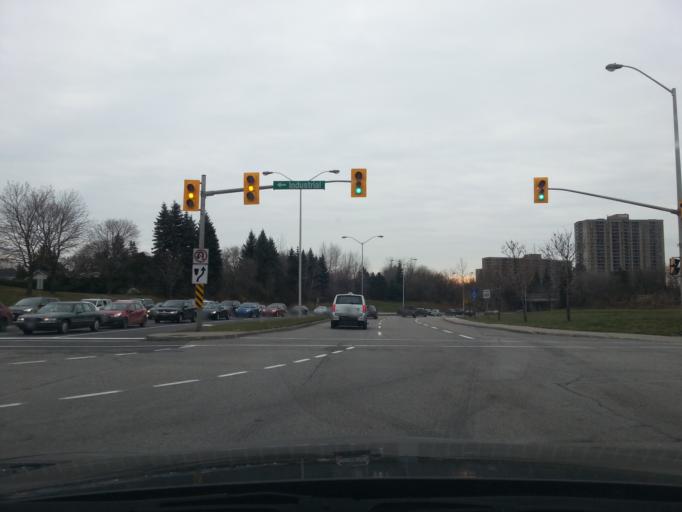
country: CA
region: Ontario
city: Ottawa
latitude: 45.4123
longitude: -75.6584
